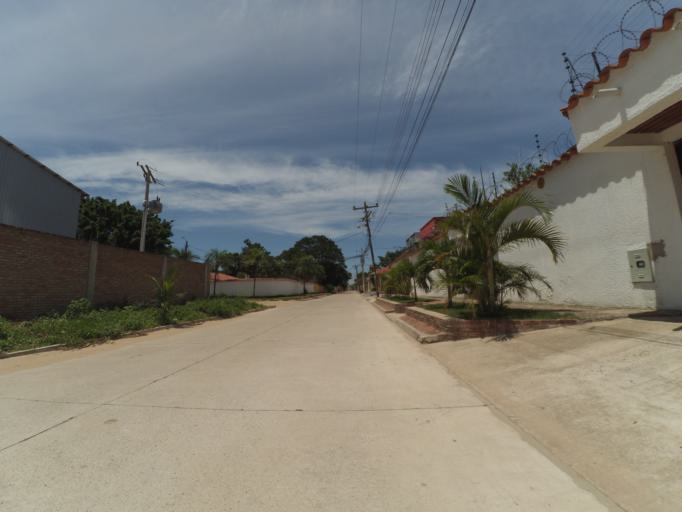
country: BO
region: Santa Cruz
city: Santa Cruz de la Sierra
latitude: -17.8116
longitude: -63.2226
